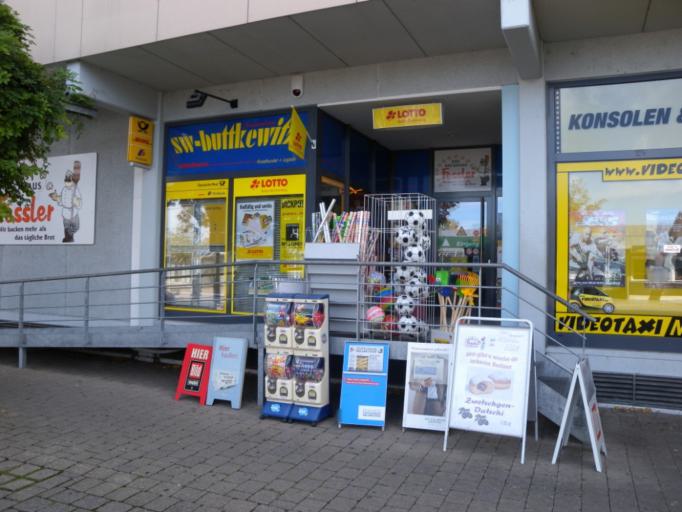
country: DE
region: Baden-Wuerttemberg
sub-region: Regierungsbezirk Stuttgart
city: Sersheim
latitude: 48.9610
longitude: 9.0634
